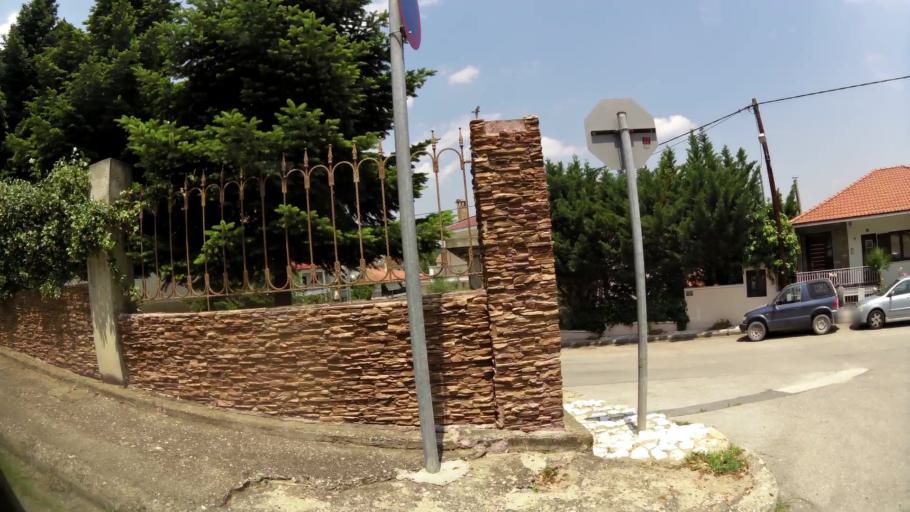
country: GR
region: Central Macedonia
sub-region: Nomos Imathias
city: Veroia
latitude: 40.5130
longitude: 22.1862
